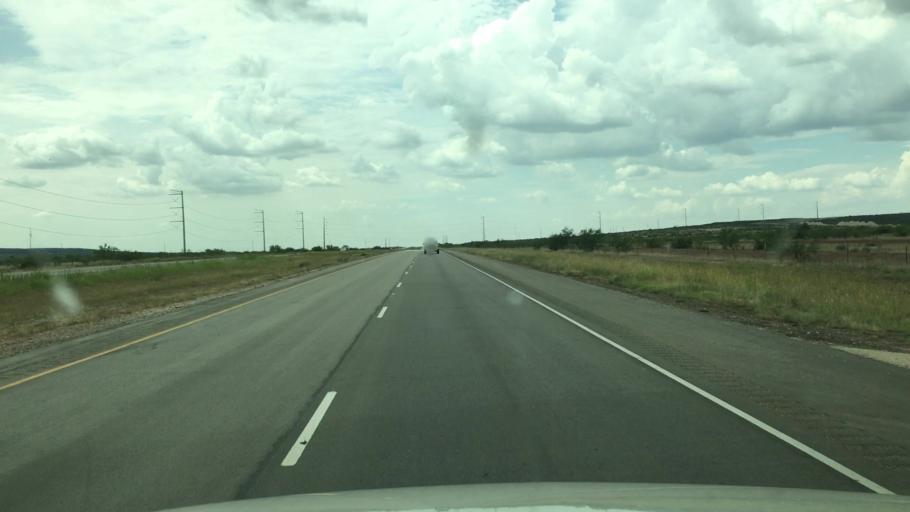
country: US
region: Texas
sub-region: Glasscock County
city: Garden City
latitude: 31.9803
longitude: -101.2543
